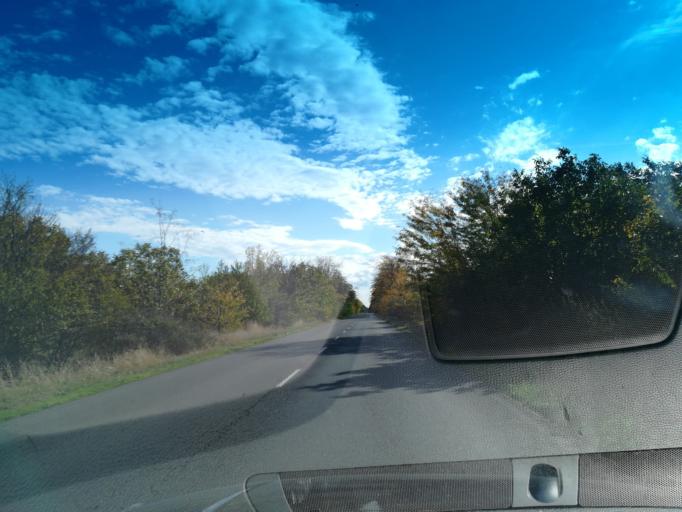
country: BG
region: Stara Zagora
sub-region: Obshtina Stara Zagora
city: Stara Zagora
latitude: 42.3784
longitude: 25.6509
